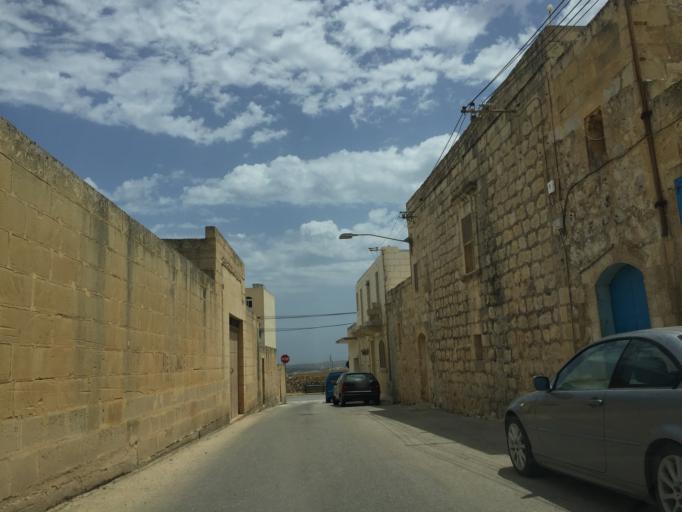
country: MT
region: Iz-Zebbug
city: Zebbug
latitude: 36.0721
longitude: 14.2366
